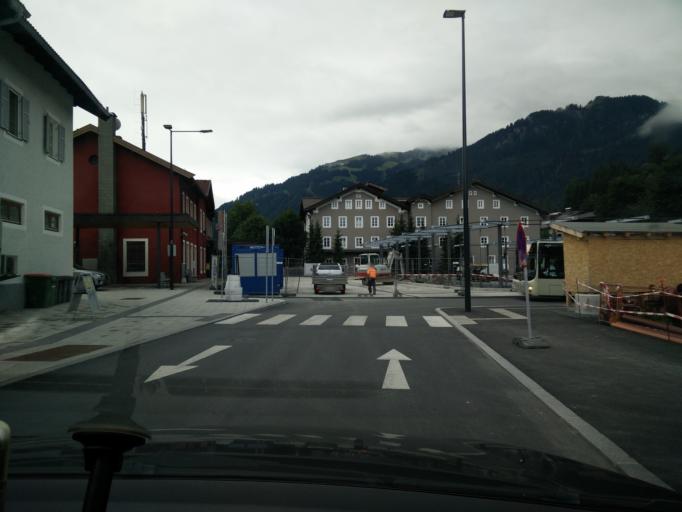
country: AT
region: Tyrol
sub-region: Politischer Bezirk Kitzbuhel
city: Kitzbuhel
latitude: 47.4547
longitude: 12.3903
